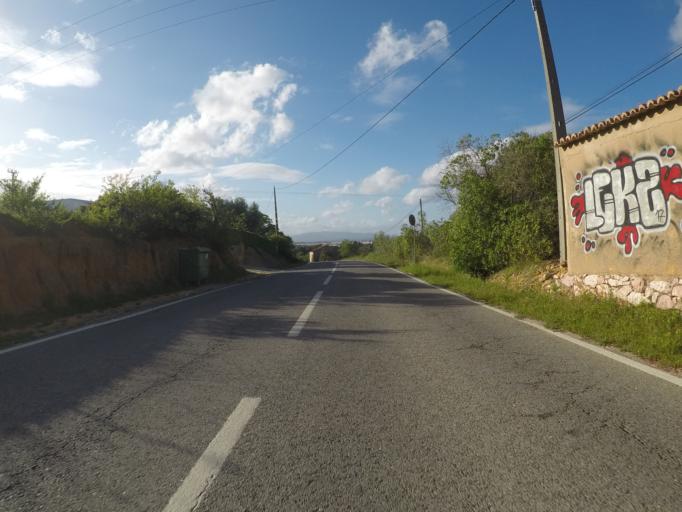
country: PT
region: Faro
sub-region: Lagoa
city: Carvoeiro
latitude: 37.1034
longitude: -8.4445
